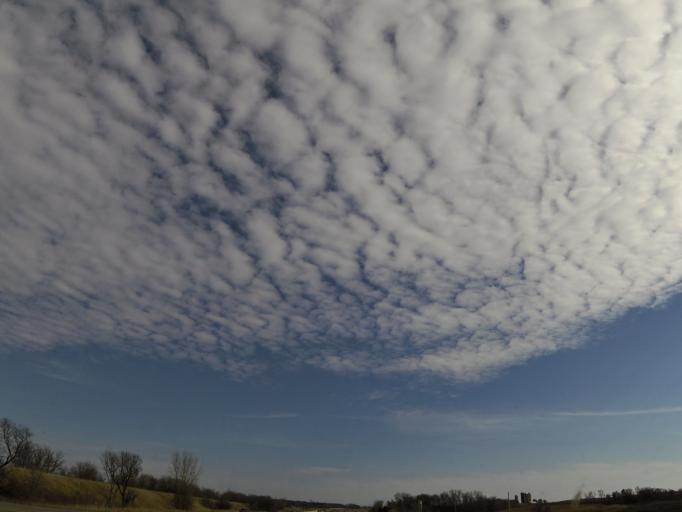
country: US
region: Minnesota
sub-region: Steele County
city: Medford
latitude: 44.2126
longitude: -93.2680
